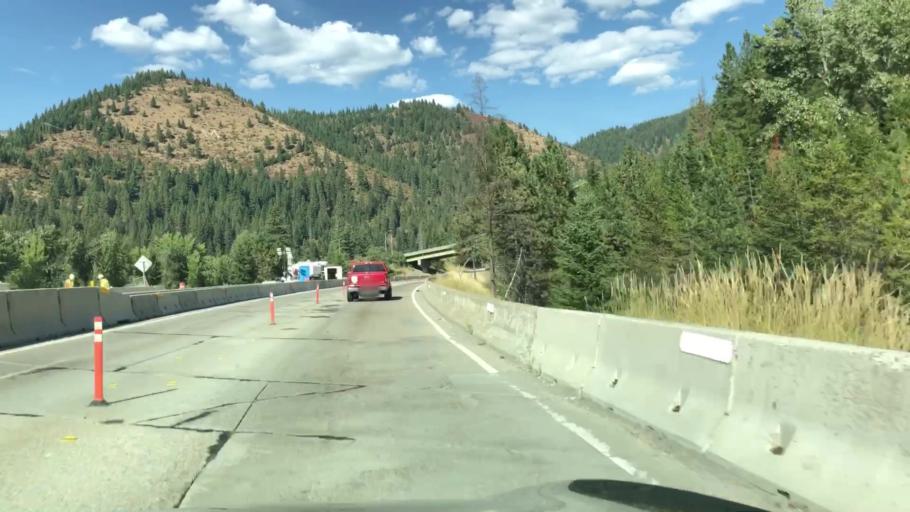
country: US
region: Idaho
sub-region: Shoshone County
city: Wallace
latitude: 47.4663
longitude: -115.8013
